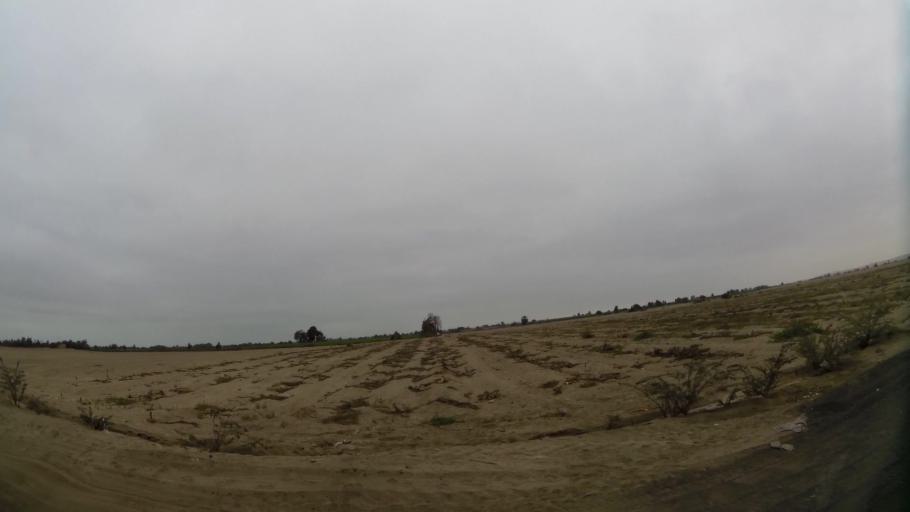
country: PE
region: Ica
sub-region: Provincia de Pisco
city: Pisco
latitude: -13.7550
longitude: -76.1838
